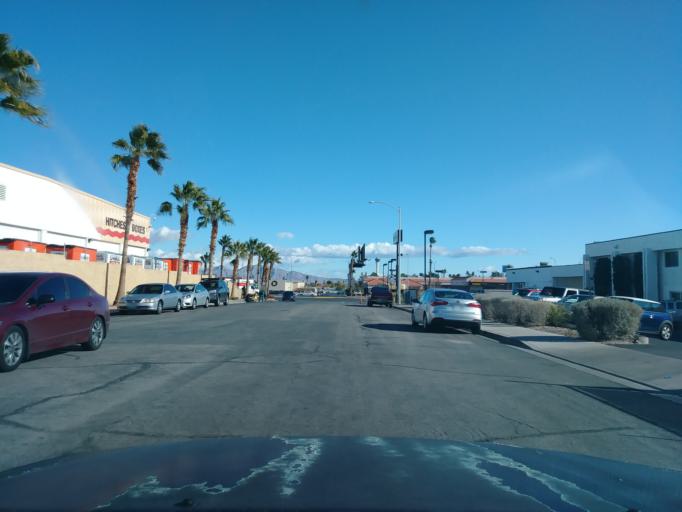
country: US
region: Nevada
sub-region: Clark County
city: Spring Valley
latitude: 36.1499
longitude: -115.2095
